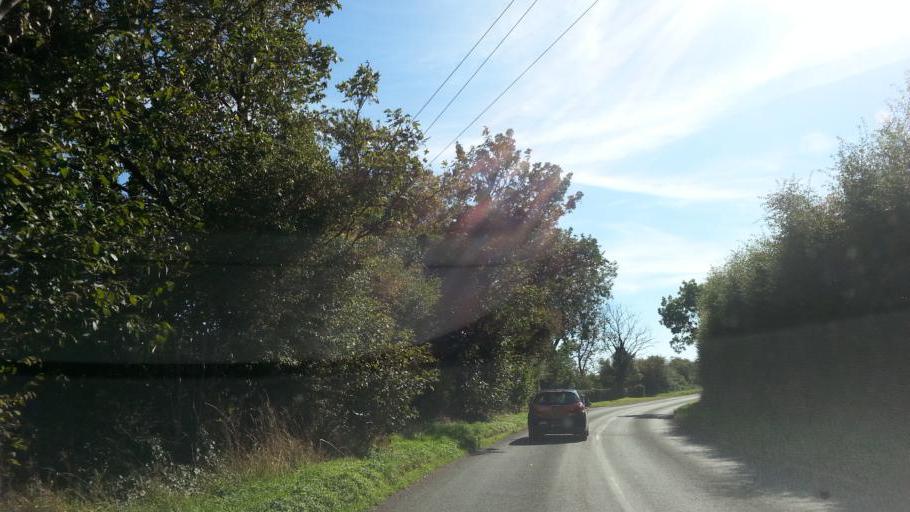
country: GB
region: England
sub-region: Staffordshire
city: Stafford
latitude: 52.7956
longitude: -2.1611
